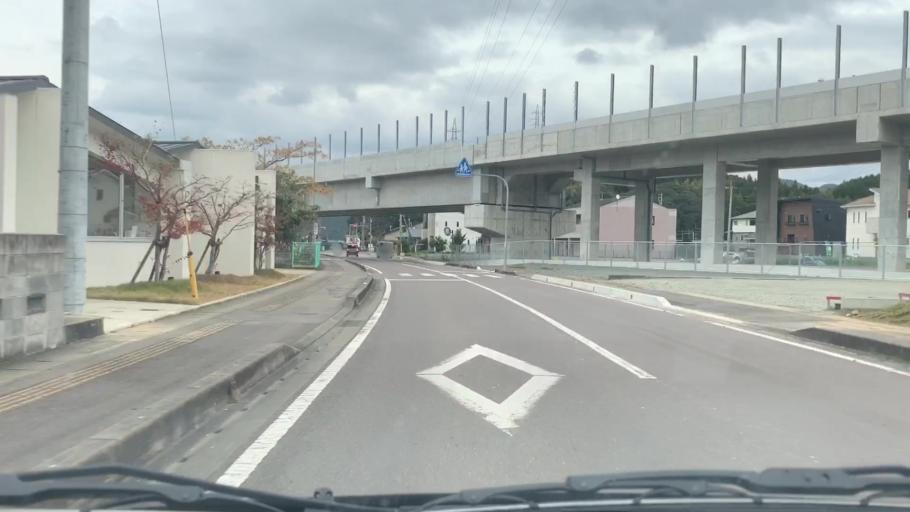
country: JP
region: Saga Prefecture
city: Ureshinomachi-shimojuku
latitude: 33.1002
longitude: 129.9979
